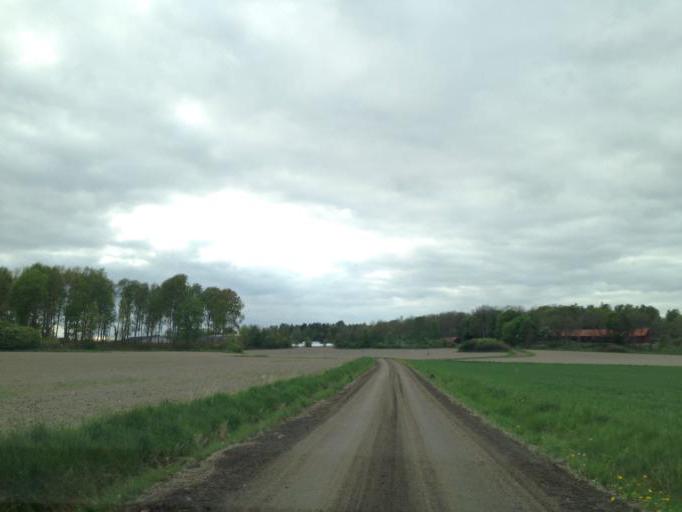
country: SE
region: Soedermanland
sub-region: Eskilstuna Kommun
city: Kvicksund
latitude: 59.4346
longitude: 16.3052
